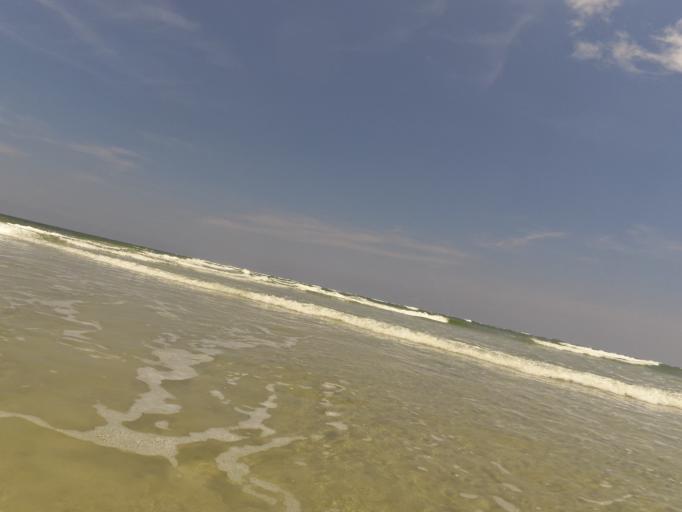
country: US
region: Florida
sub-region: Duval County
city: Atlantic Beach
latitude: 30.4348
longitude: -81.4044
